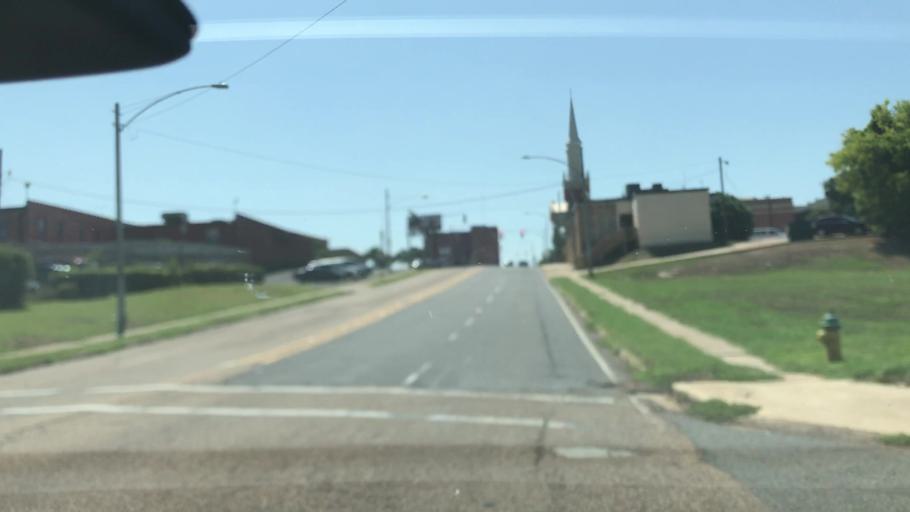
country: US
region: Louisiana
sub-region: Caddo Parish
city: Shreveport
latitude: 32.5125
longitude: -93.7544
